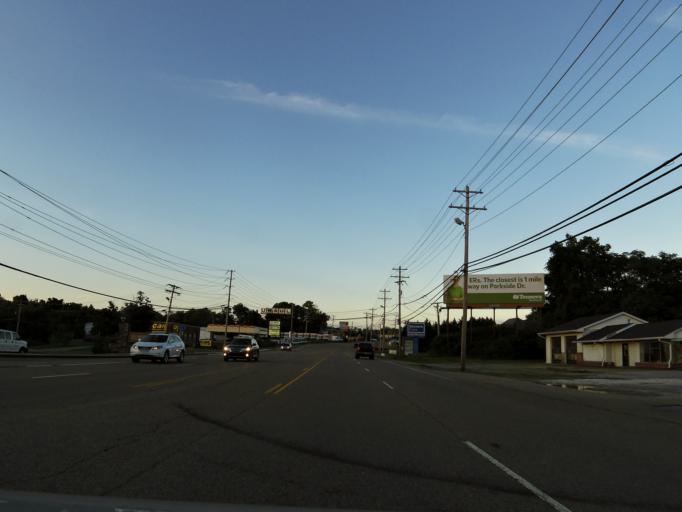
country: US
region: Tennessee
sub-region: Knox County
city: Farragut
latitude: 35.8919
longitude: -84.1454
